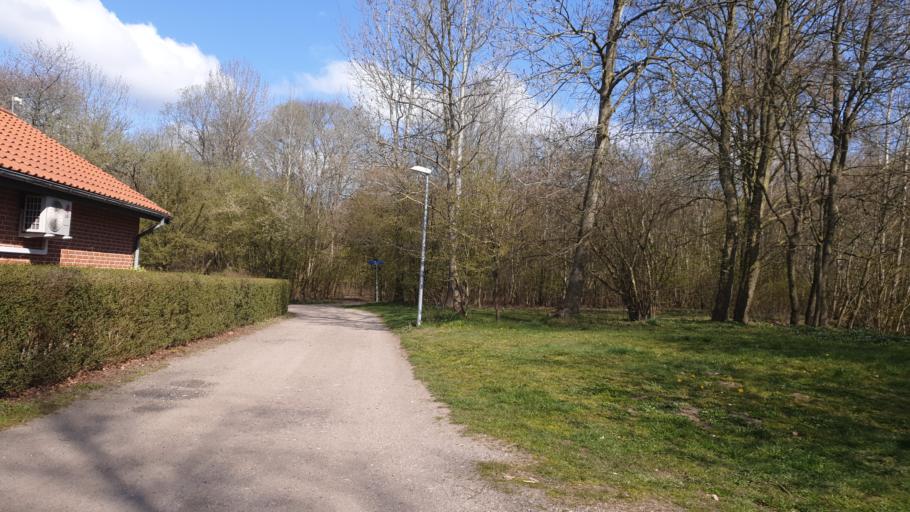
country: DK
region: Central Jutland
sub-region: Hedensted Kommune
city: Hedensted
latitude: 55.8079
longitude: 9.6990
